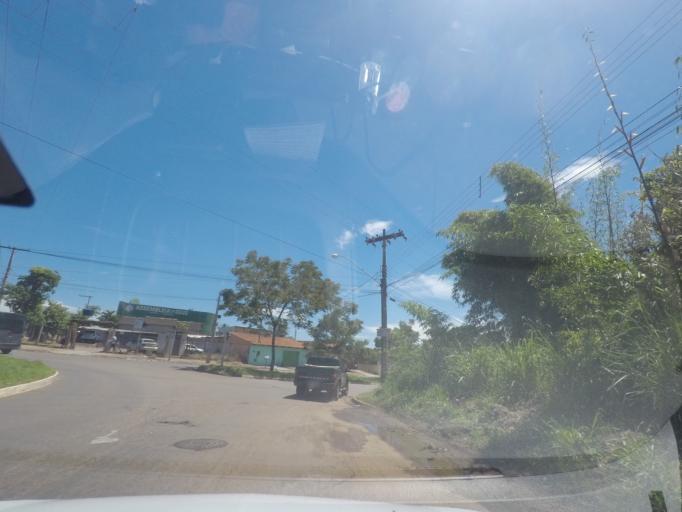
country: BR
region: Goias
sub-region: Aparecida De Goiania
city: Aparecida de Goiania
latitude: -16.7758
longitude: -49.3292
